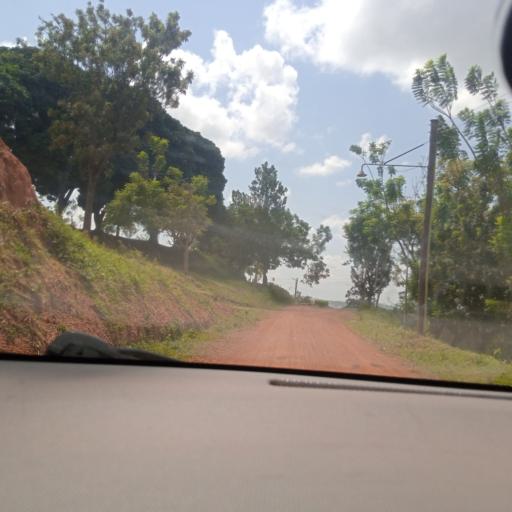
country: UG
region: Central Region
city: Masaka
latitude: -0.3238
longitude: 31.7418
